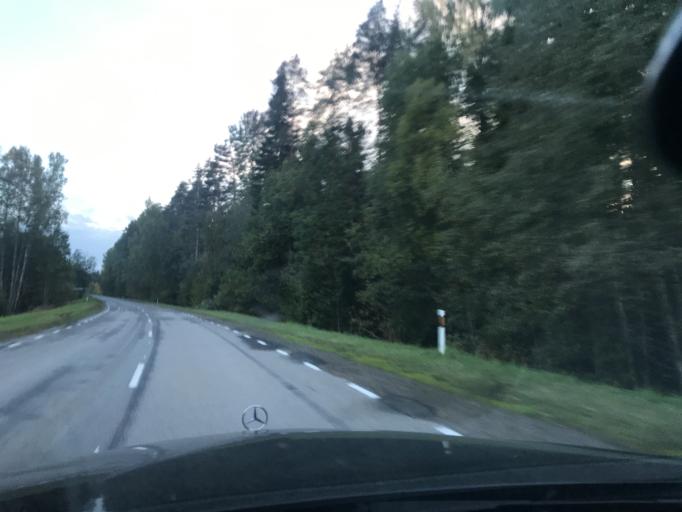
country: EE
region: Valgamaa
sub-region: Torva linn
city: Torva
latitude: 58.0033
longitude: 26.0809
